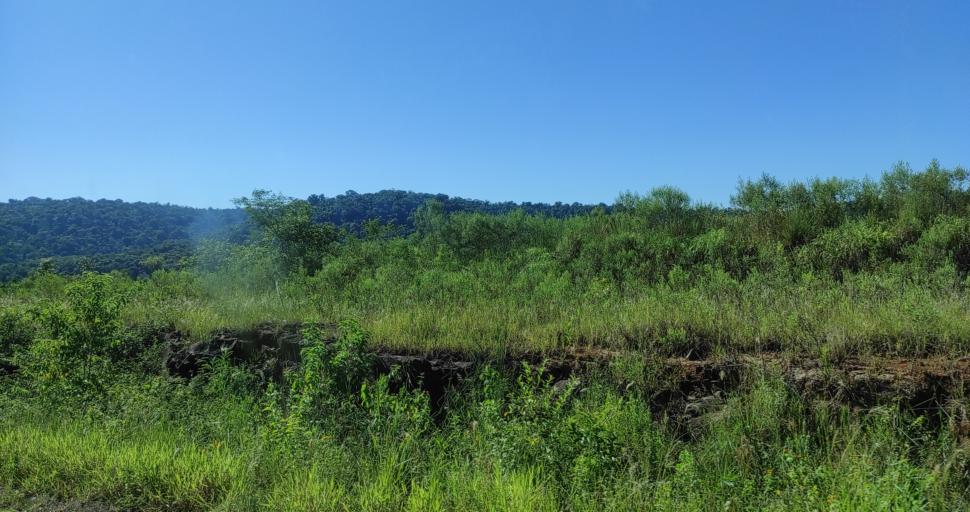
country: AR
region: Misiones
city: El Soberbio
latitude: -27.2467
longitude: -54.0283
